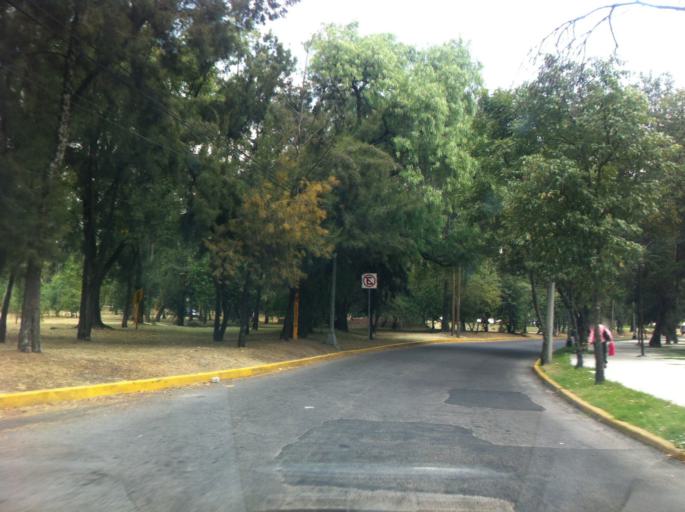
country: MX
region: Mexico City
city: Polanco
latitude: 19.4250
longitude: -99.1996
